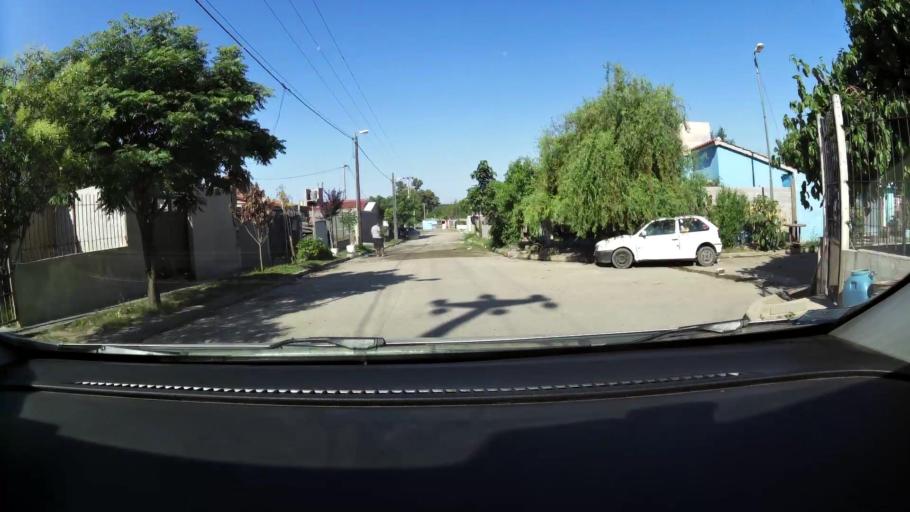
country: AR
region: Cordoba
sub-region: Departamento de Capital
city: Cordoba
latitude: -31.4022
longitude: -64.1501
